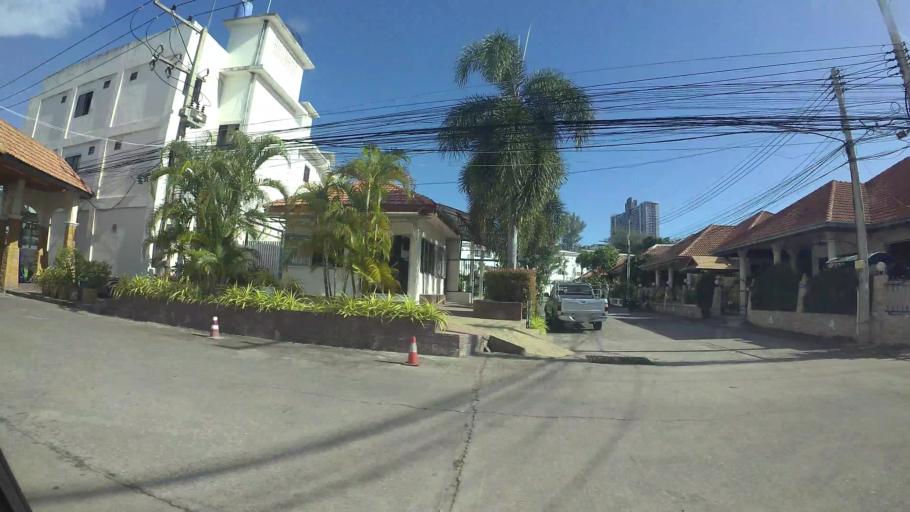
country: TH
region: Chon Buri
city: Phatthaya
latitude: 12.9119
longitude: 100.8798
